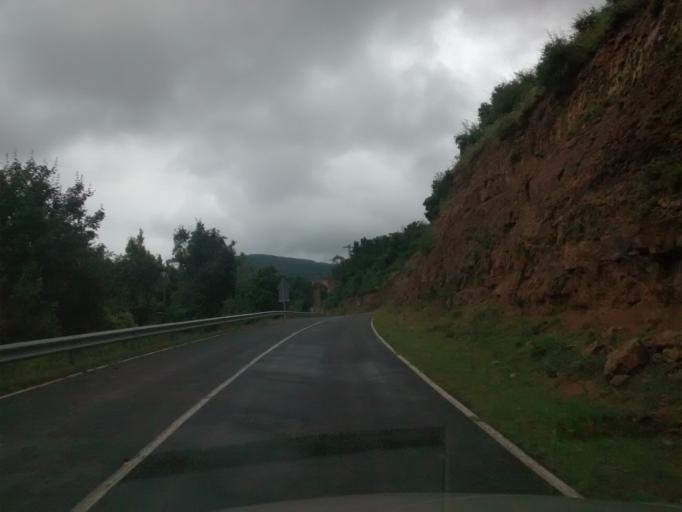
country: ES
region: La Rioja
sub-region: Provincia de La Rioja
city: Ajamil
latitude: 42.1702
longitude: -2.4853
